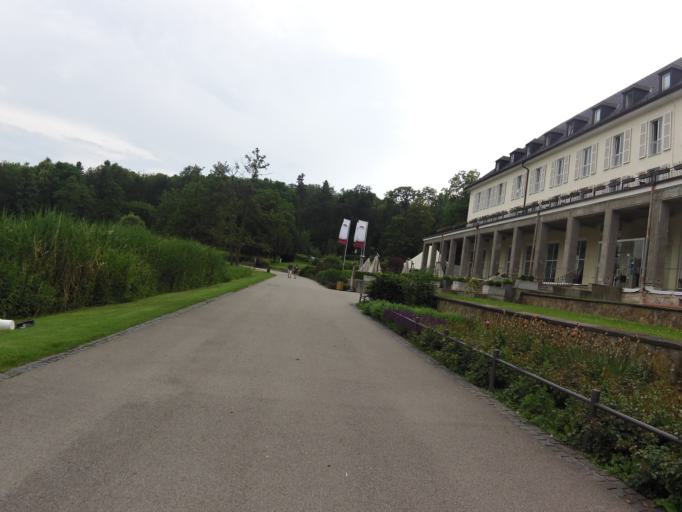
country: DE
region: Thuringia
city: Bad Salzungen
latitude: 50.8107
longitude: 10.2350
